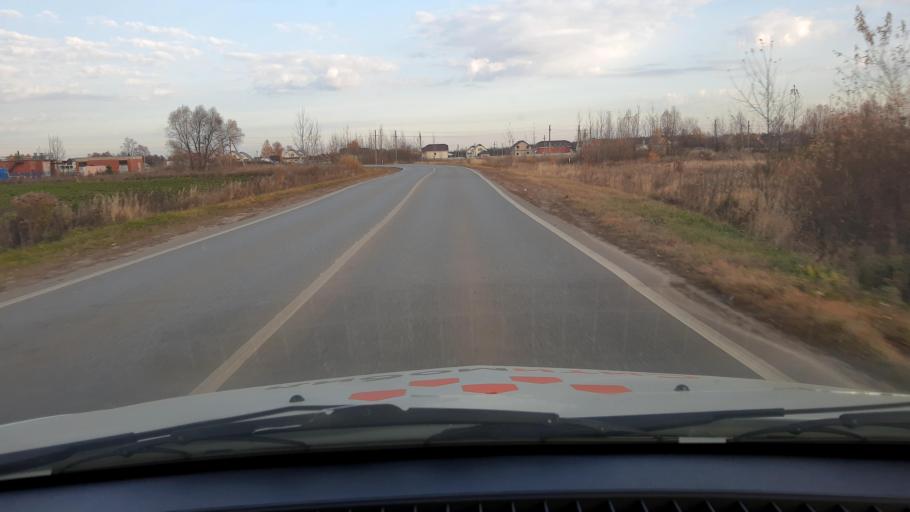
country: RU
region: Bashkortostan
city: Kabakovo
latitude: 54.7422
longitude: 56.2023
